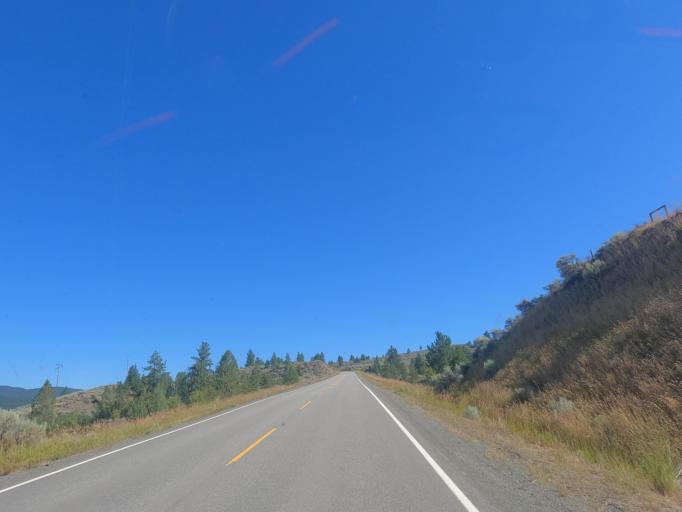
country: CA
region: British Columbia
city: Merritt
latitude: 50.1885
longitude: -120.8524
